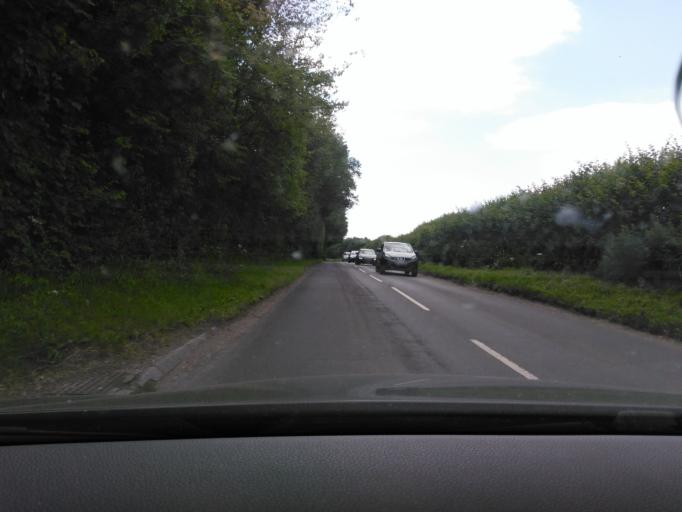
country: GB
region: England
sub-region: Hampshire
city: Andover
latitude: 51.1976
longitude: -1.5072
